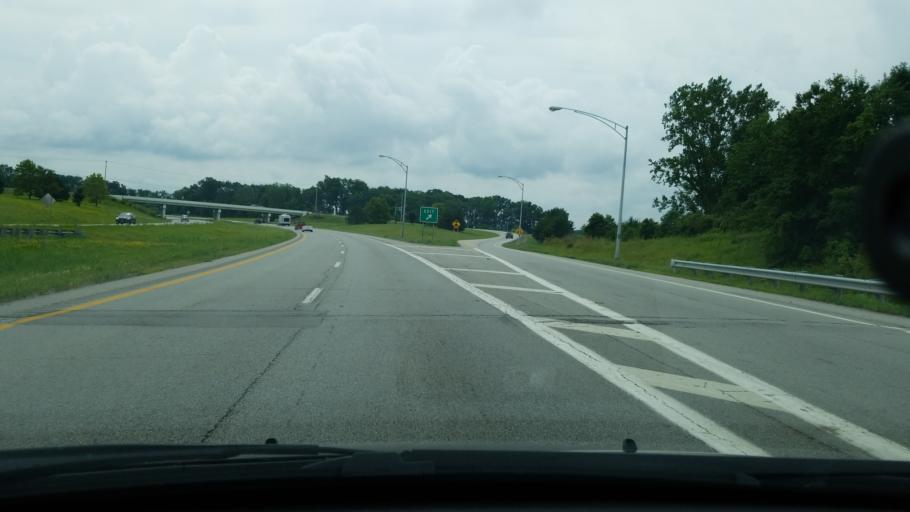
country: US
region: Ohio
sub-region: Erie County
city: Huron
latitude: 41.3732
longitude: -82.5718
